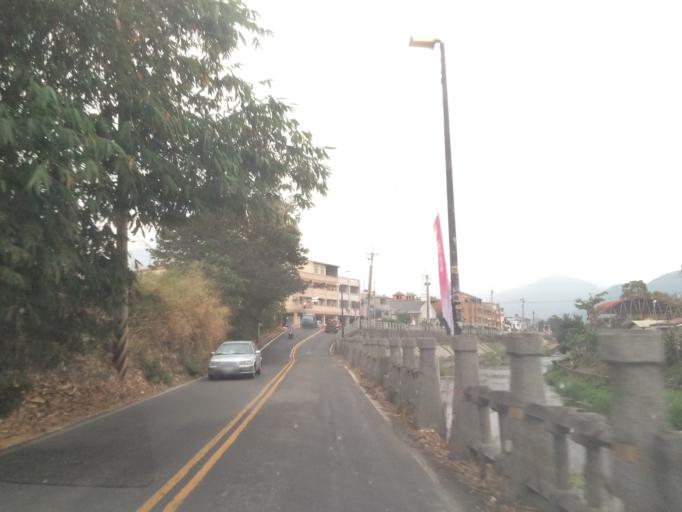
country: TW
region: Taiwan
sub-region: Nantou
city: Puli
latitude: 23.9638
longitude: 120.9586
